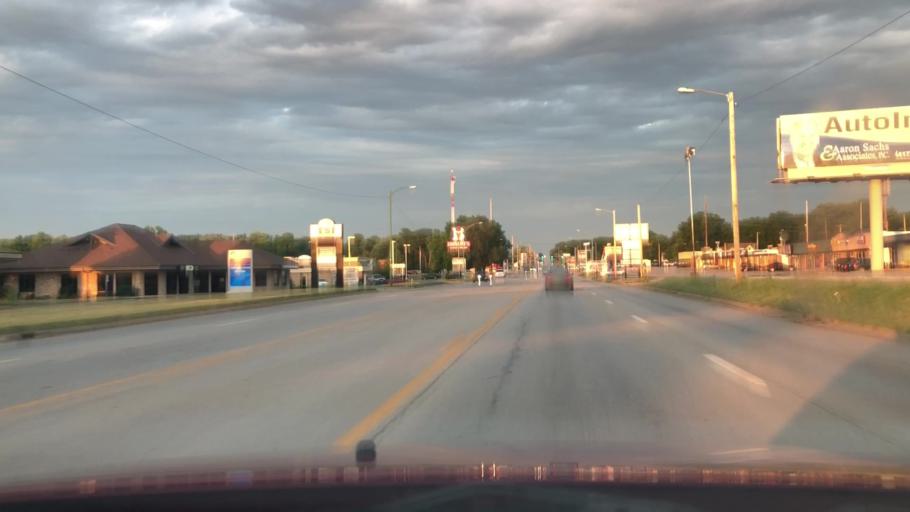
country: US
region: Missouri
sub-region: Greene County
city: Springfield
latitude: 37.1823
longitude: -93.3122
